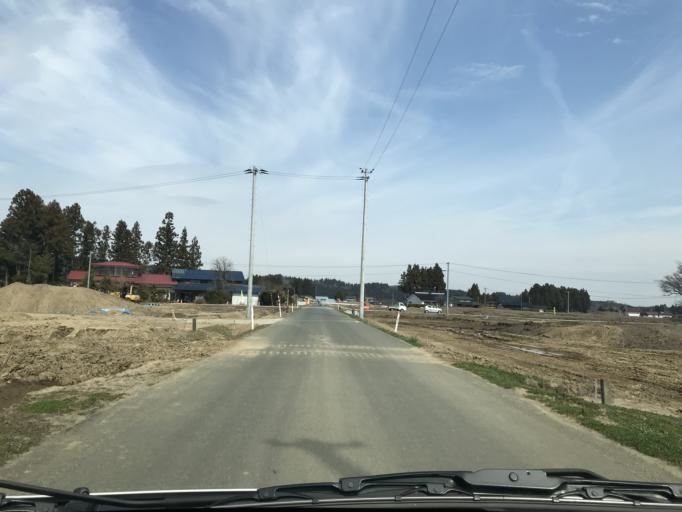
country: JP
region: Iwate
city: Mizusawa
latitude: 39.1353
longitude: 141.0473
